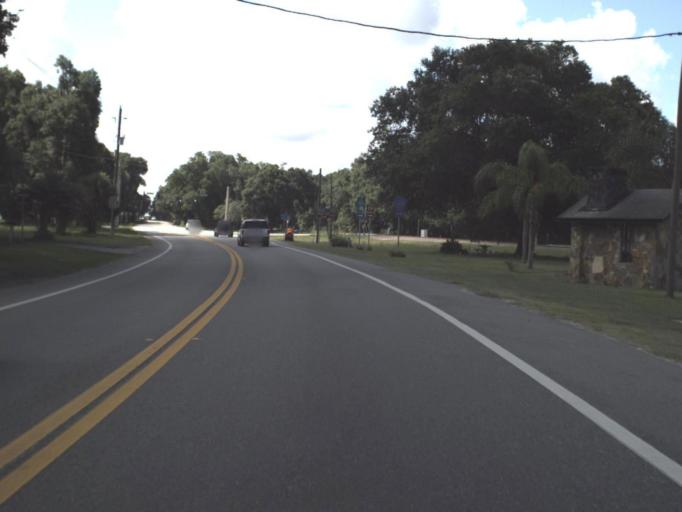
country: US
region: Florida
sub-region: Putnam County
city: Palatka
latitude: 29.5539
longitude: -81.6560
